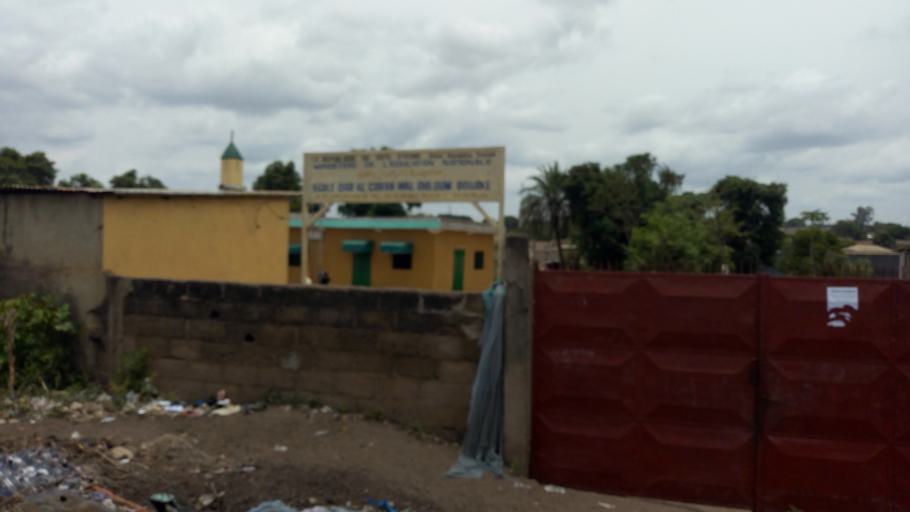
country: CI
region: Vallee du Bandama
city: Bouake
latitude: 7.6959
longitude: -5.0353
